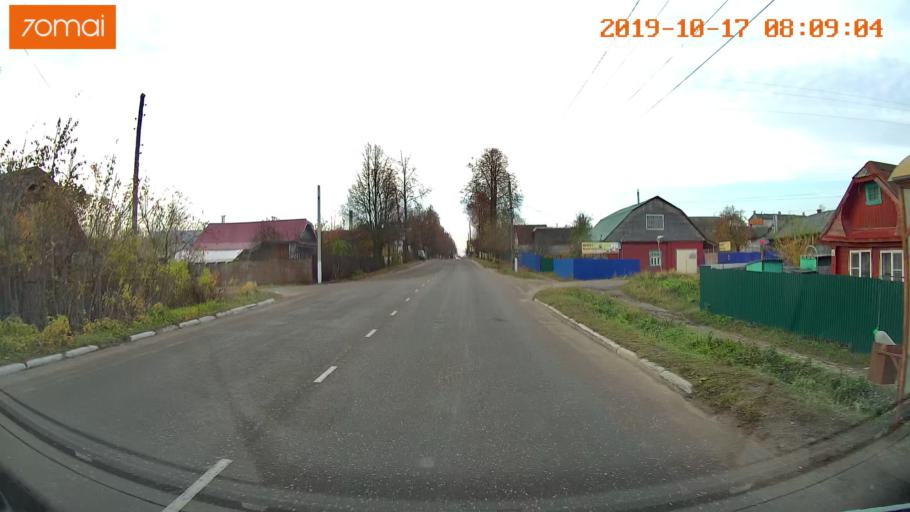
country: RU
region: Vladimir
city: Kol'chugino
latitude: 56.3146
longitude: 39.3821
